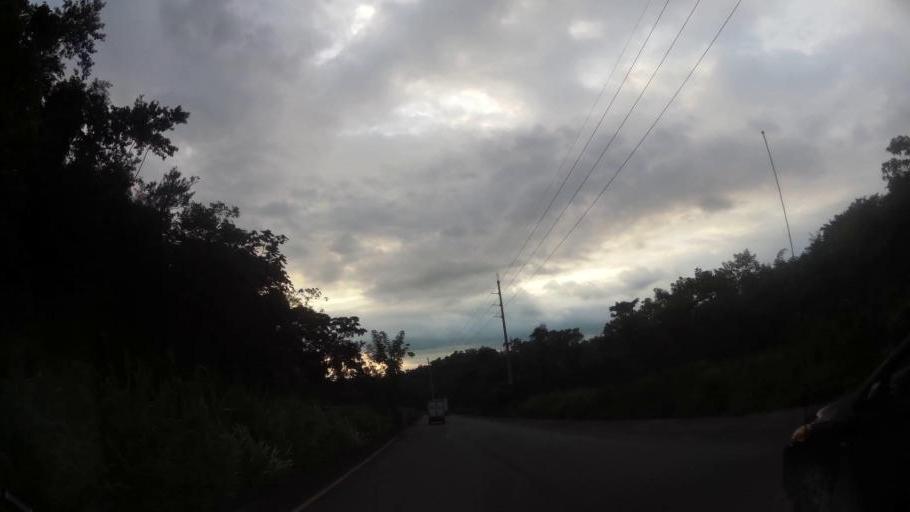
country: GT
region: Suchitepeque
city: Patulul
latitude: 14.3634
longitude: -91.0981
